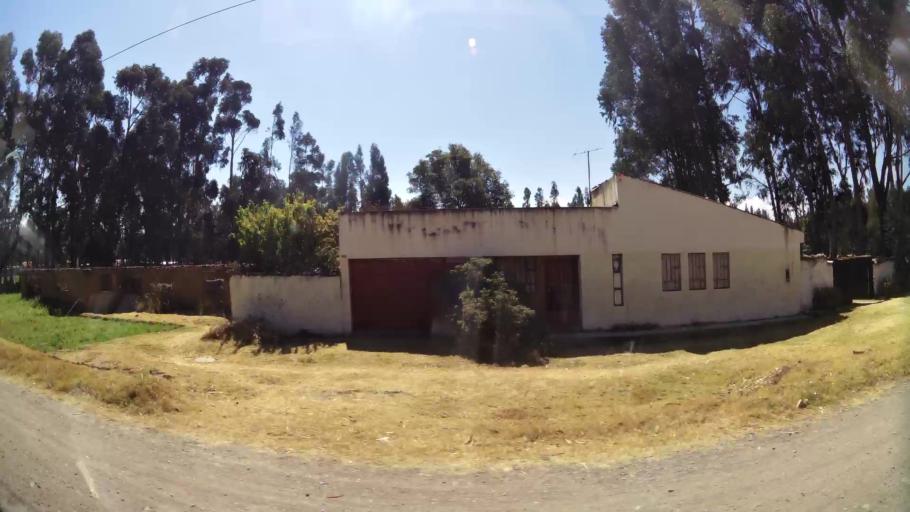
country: PE
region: Junin
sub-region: Provincia de Concepcion
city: Matahuasi
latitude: -11.9071
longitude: -75.3310
